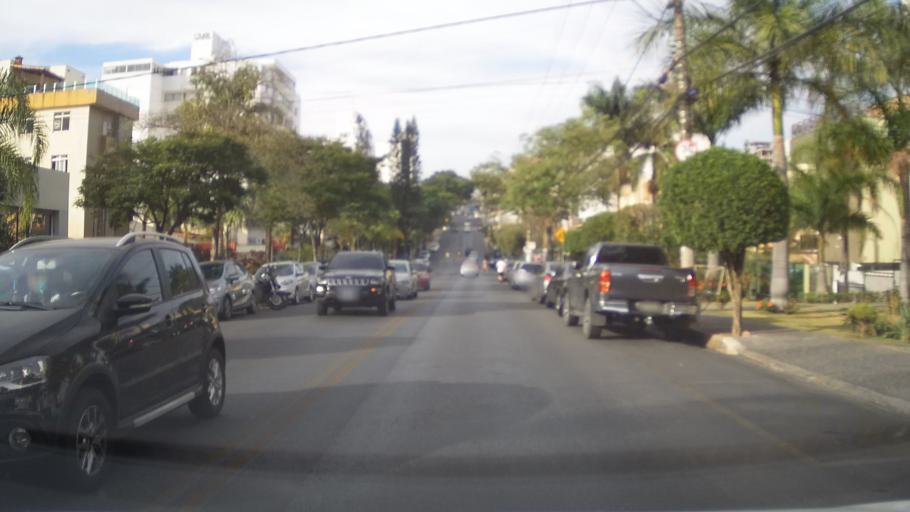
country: BR
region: Minas Gerais
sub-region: Belo Horizonte
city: Belo Horizonte
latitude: -19.8776
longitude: -43.9962
